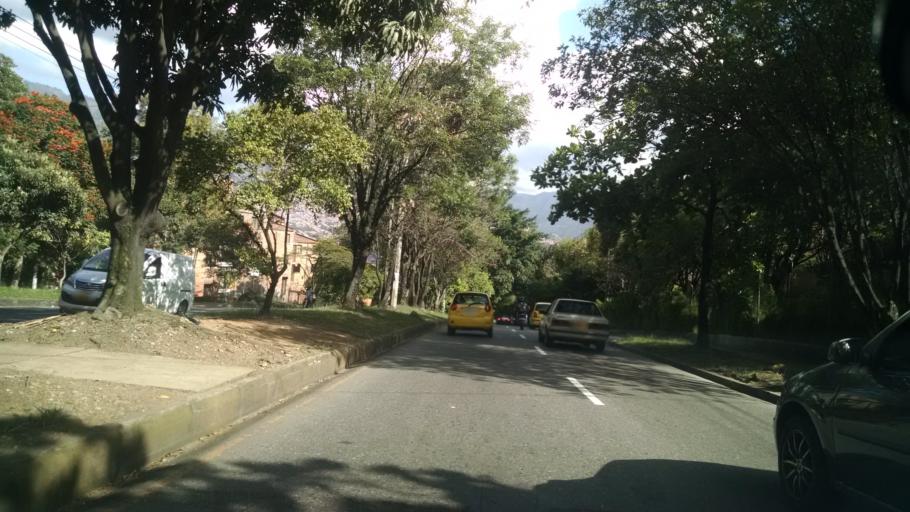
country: CO
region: Antioquia
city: Medellin
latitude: 6.2821
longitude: -75.5813
